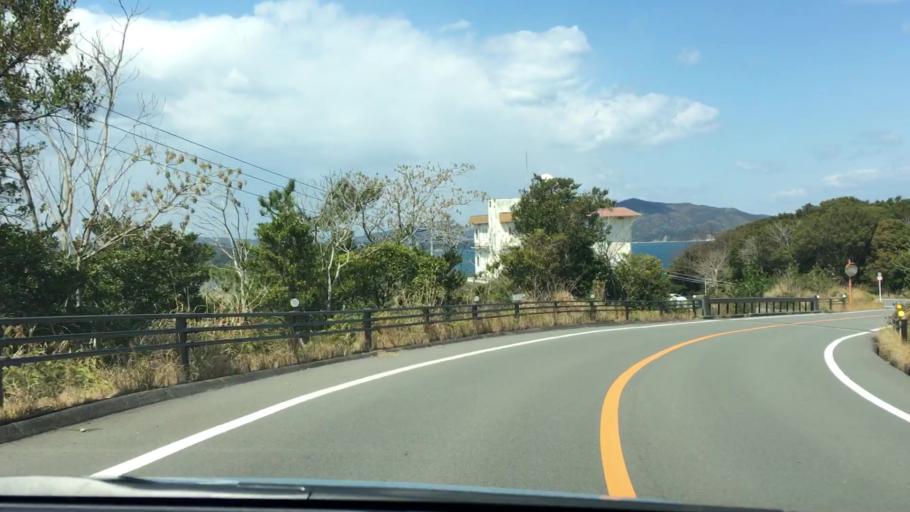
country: JP
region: Mie
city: Toba
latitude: 34.4475
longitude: 136.9110
